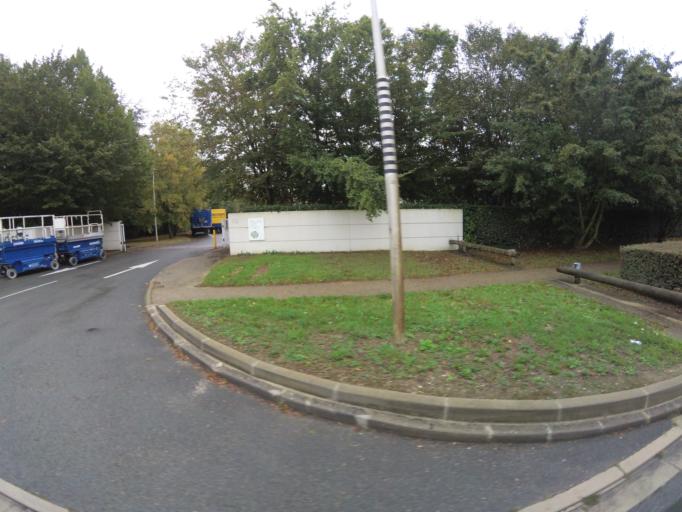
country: FR
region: Ile-de-France
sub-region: Departement de Seine-et-Marne
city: Ferrieres-en-Brie
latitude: 48.8321
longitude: 2.7193
